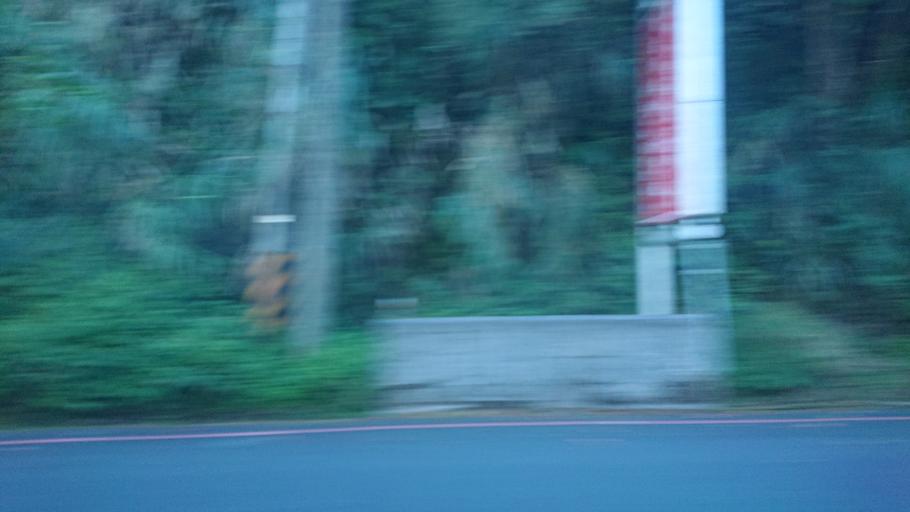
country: TW
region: Taiwan
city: Lugu
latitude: 23.5052
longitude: 120.7976
